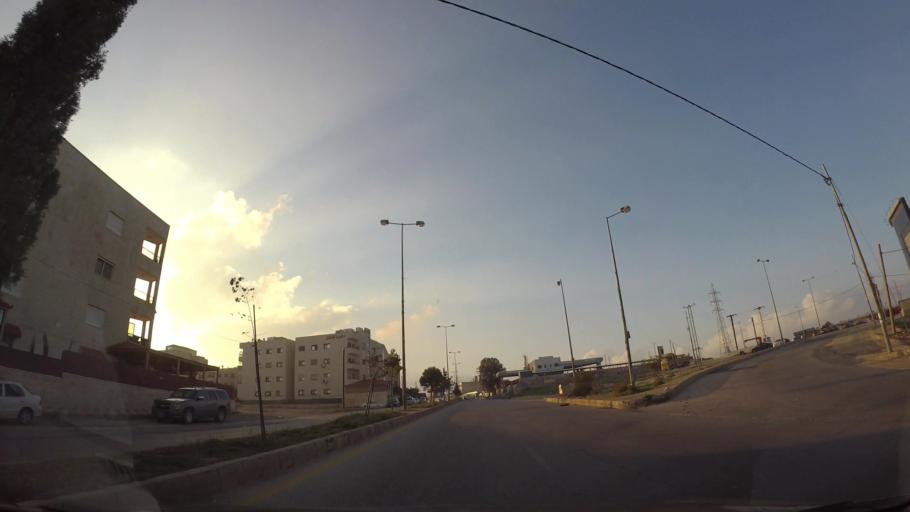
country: JO
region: Amman
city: Amman
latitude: 31.9869
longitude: 35.9506
